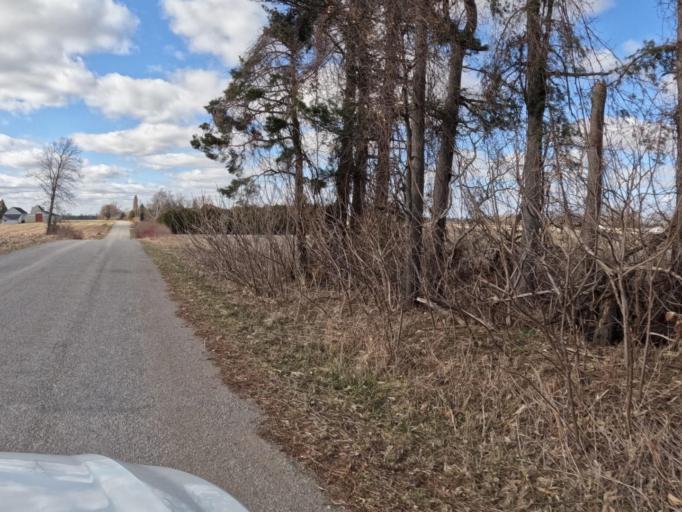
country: CA
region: Ontario
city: Norfolk County
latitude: 42.7521
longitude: -80.3009
